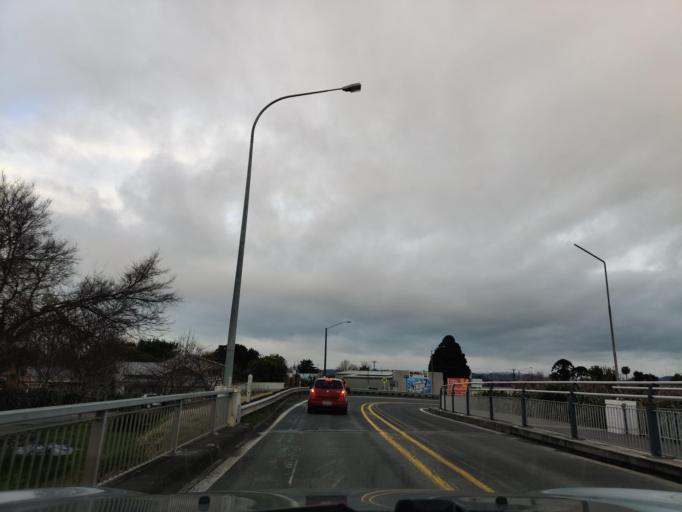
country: NZ
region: Hawke's Bay
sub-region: Napier City
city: Taradale
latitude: -39.5818
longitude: 176.9162
